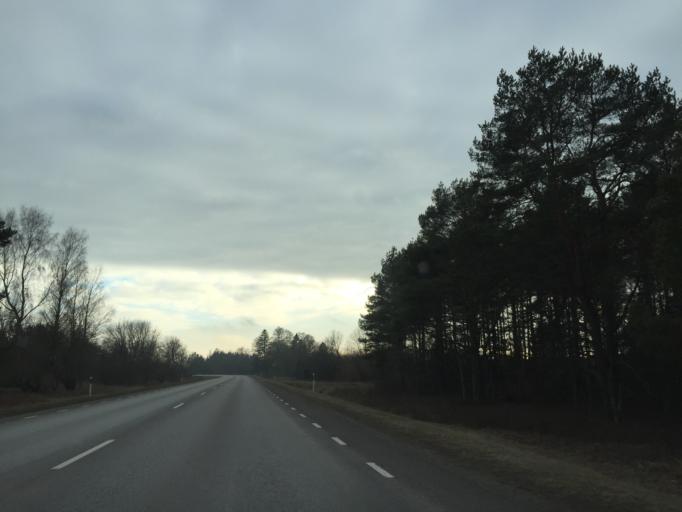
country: EE
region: Saare
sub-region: Orissaare vald
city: Orissaare
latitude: 58.4433
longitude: 22.7928
